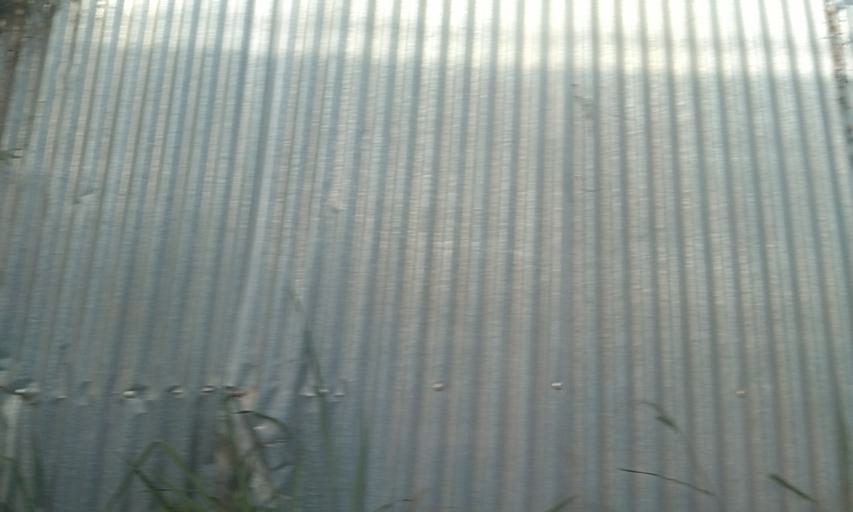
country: UG
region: Central Region
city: Kampala Central Division
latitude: 0.3509
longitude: 32.6011
